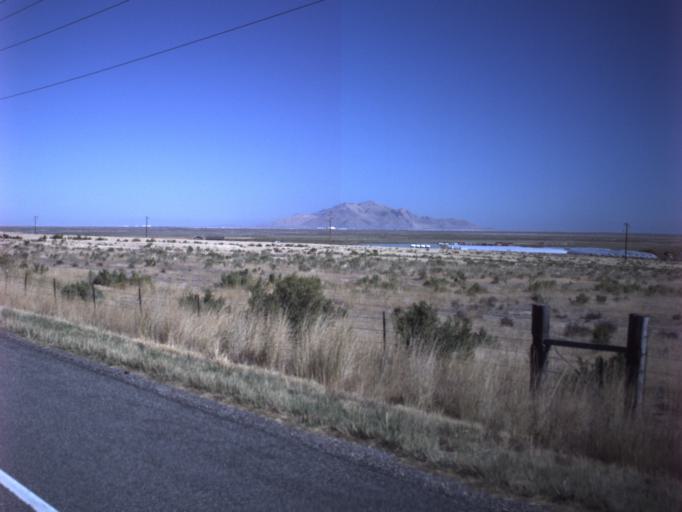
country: US
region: Utah
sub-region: Tooele County
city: Grantsville
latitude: 40.6252
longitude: -112.5077
